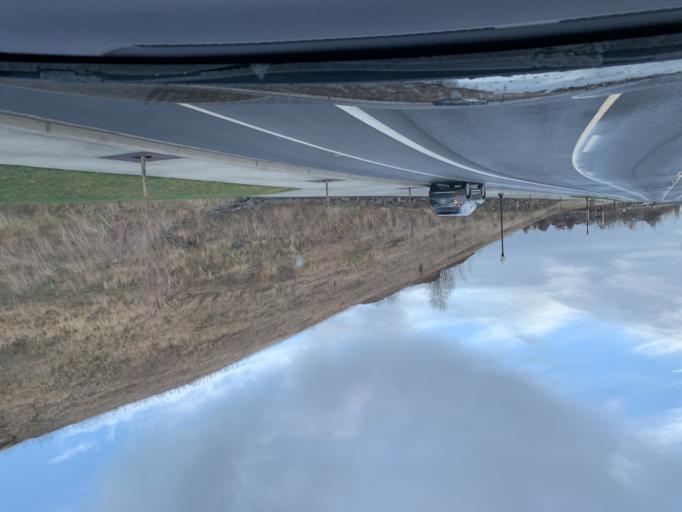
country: US
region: Washington
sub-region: Clark County
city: Mill Plain
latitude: 45.5891
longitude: -122.4715
